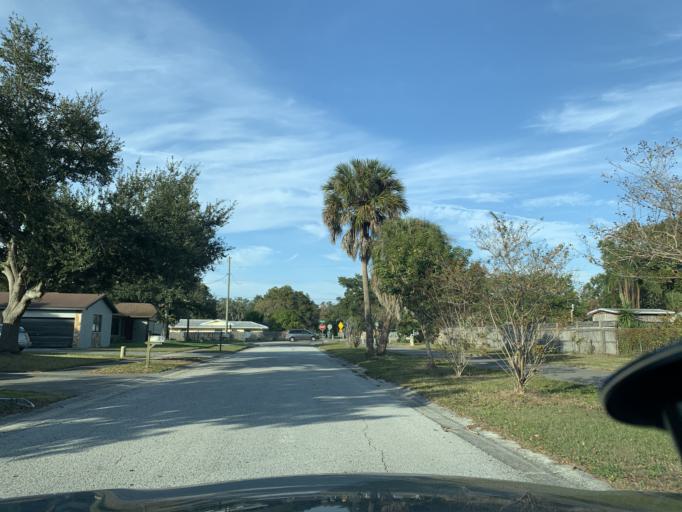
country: US
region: Florida
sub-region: Pinellas County
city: Ridgecrest
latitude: 27.9014
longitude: -82.7996
